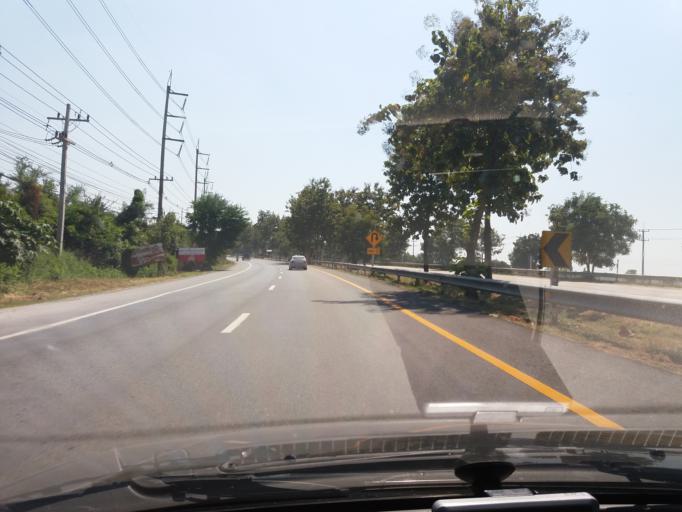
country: TH
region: Chai Nat
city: Sankhaburi
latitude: 15.1048
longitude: 100.1365
